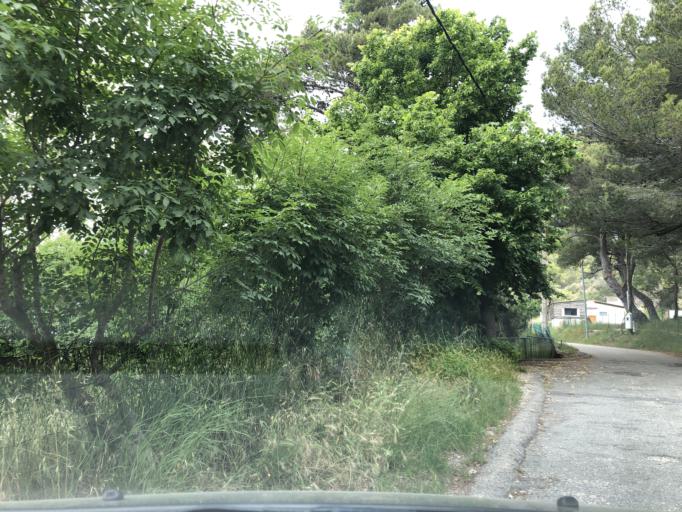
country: FR
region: Provence-Alpes-Cote d'Azur
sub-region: Departement des Alpes-Maritimes
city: Eze
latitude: 43.7362
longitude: 7.3440
